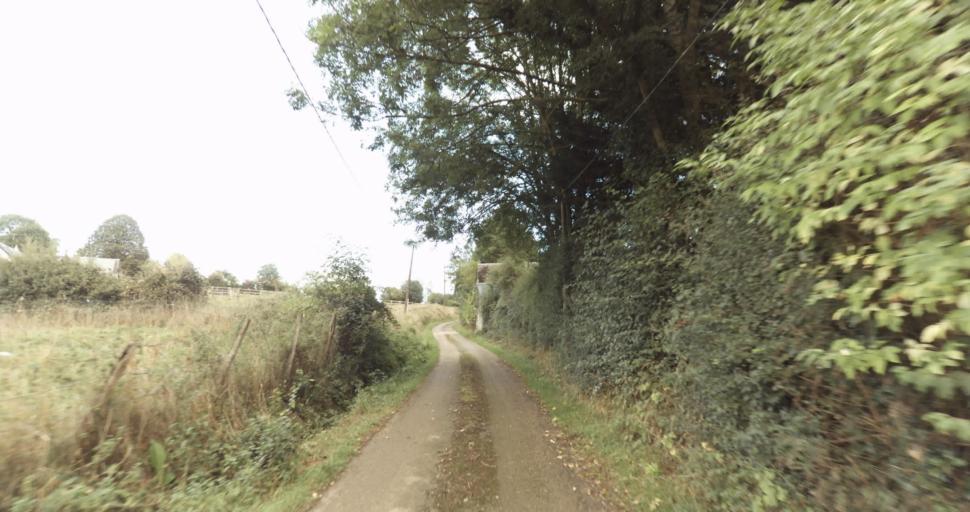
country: FR
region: Lower Normandy
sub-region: Departement de l'Orne
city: Gace
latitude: 48.7691
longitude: 0.3260
